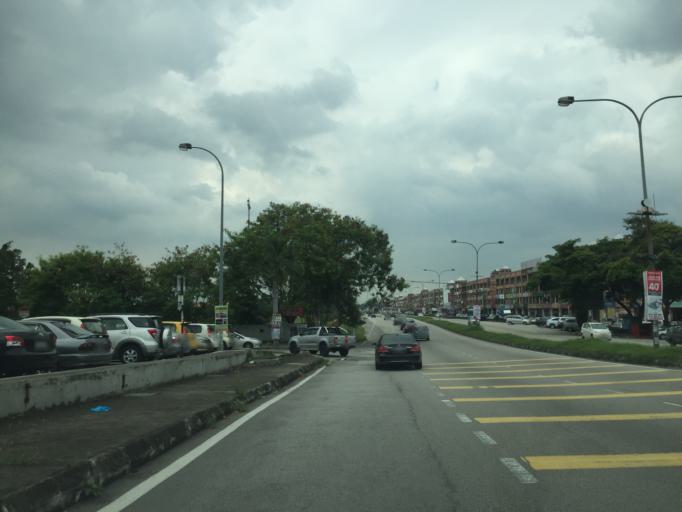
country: MY
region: Selangor
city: Klang
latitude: 3.0138
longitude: 101.4389
